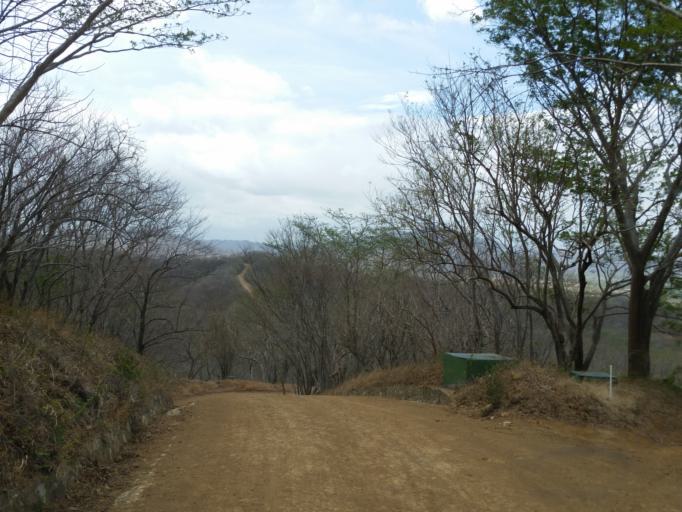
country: NI
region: Rivas
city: Tola
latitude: 11.4179
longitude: -86.0661
